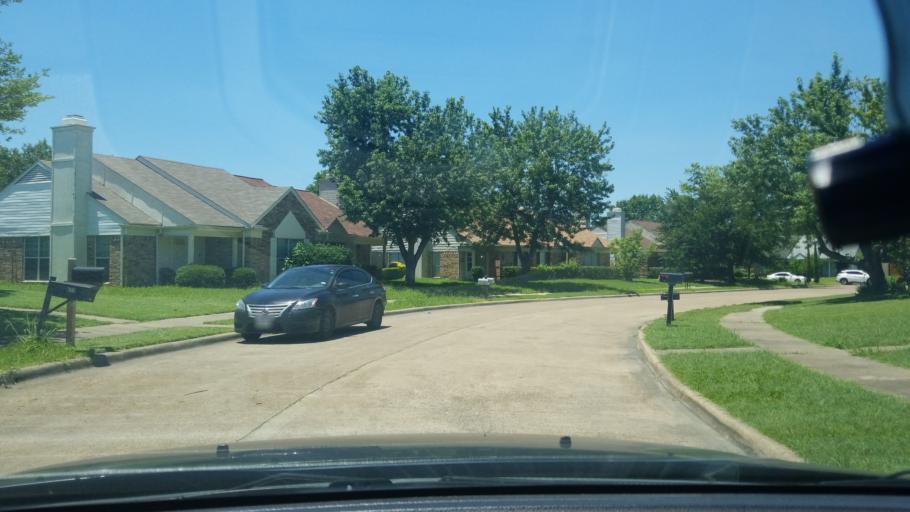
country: US
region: Texas
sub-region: Dallas County
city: Mesquite
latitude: 32.7735
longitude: -96.6066
